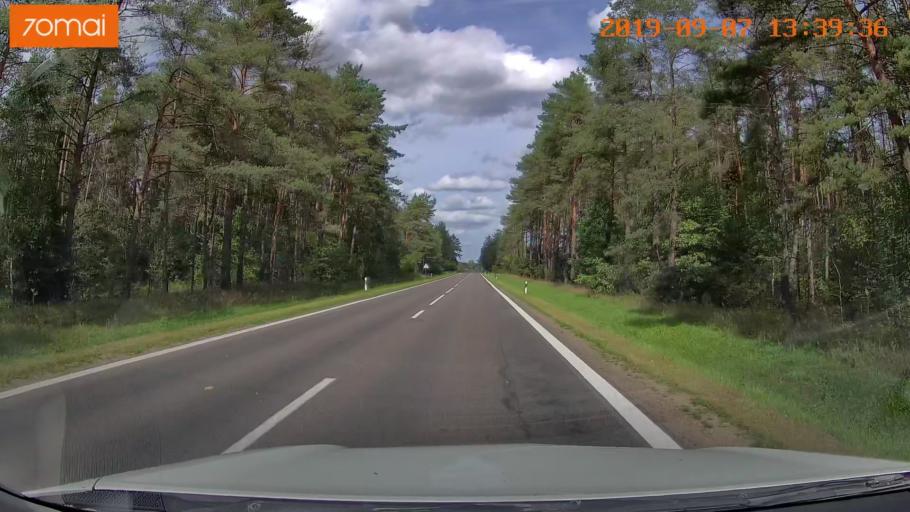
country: LT
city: Skaidiskes
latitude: 54.5706
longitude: 25.3160
